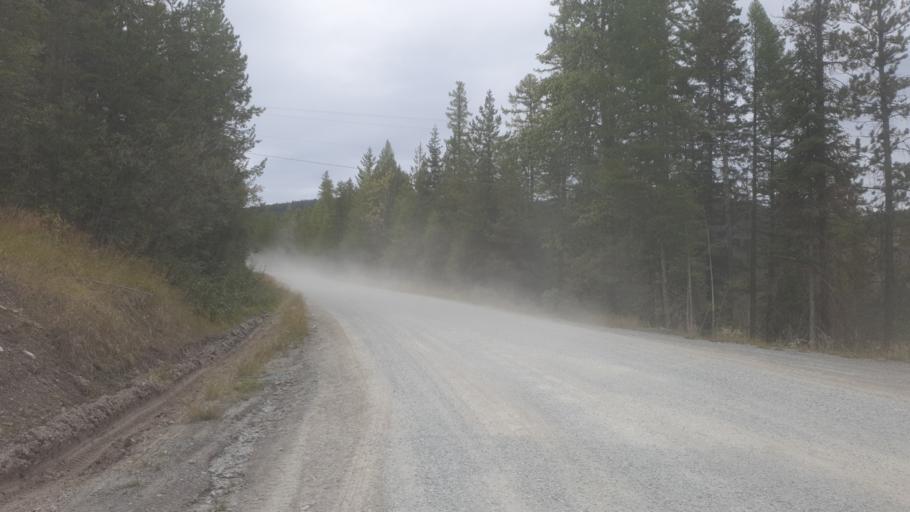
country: US
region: Montana
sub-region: Flathead County
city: Lakeside
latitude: 47.9938
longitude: -114.3212
